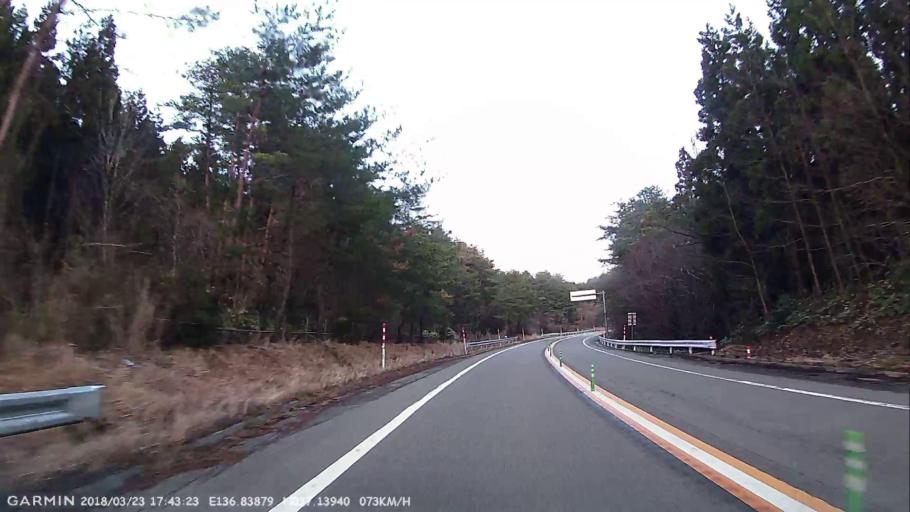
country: JP
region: Ishikawa
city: Nanao
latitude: 37.1394
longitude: 136.8391
